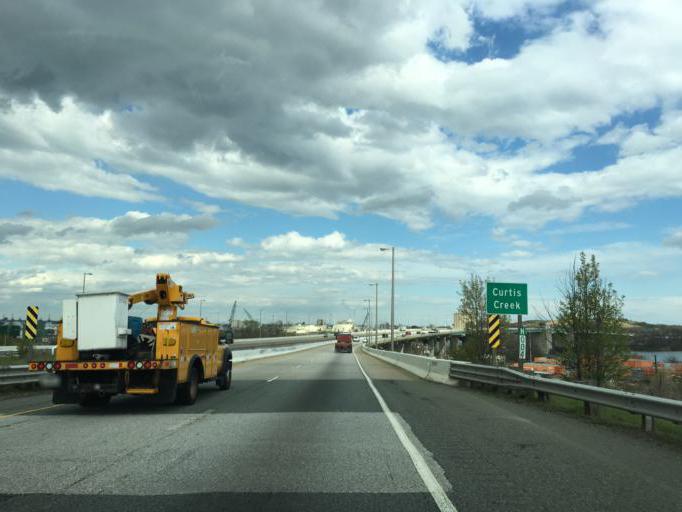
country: US
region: Maryland
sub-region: Anne Arundel County
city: Brooklyn Park
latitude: 39.2064
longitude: -76.5883
